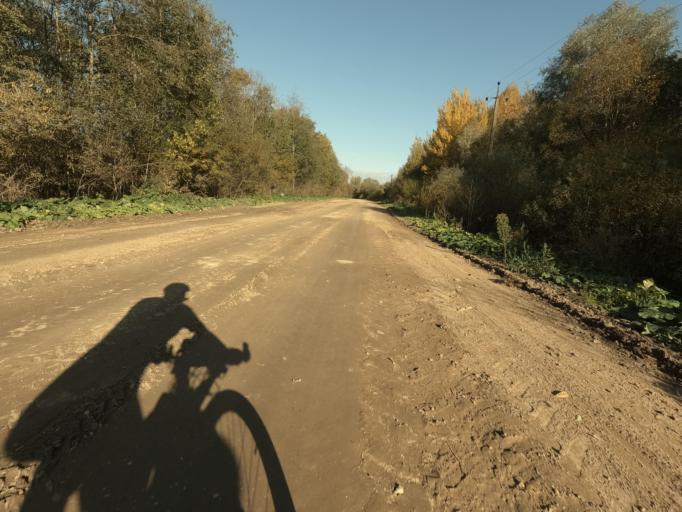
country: RU
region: Novgorod
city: Batetskiy
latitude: 58.8781
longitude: 30.7267
